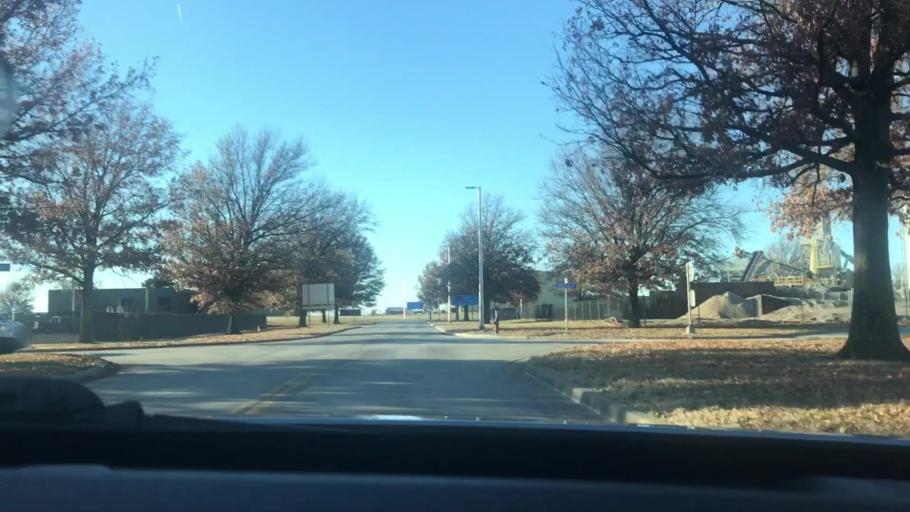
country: US
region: Missouri
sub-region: Platte County
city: Weatherby Lake
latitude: 39.3124
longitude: -94.7142
